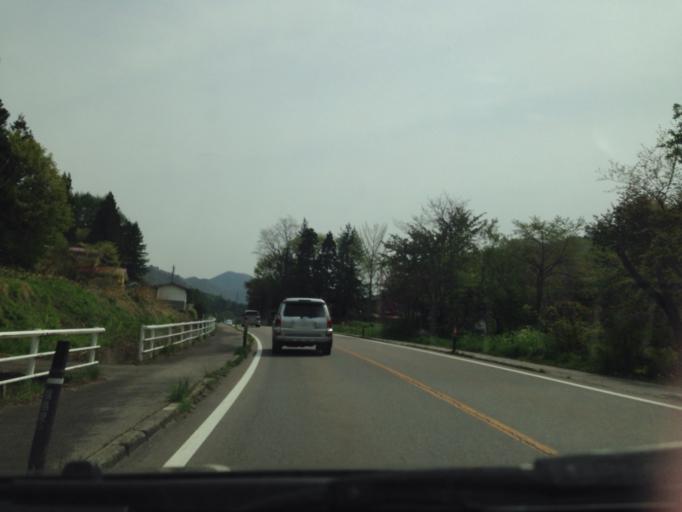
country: JP
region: Tochigi
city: Kuroiso
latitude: 37.1332
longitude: 139.7179
